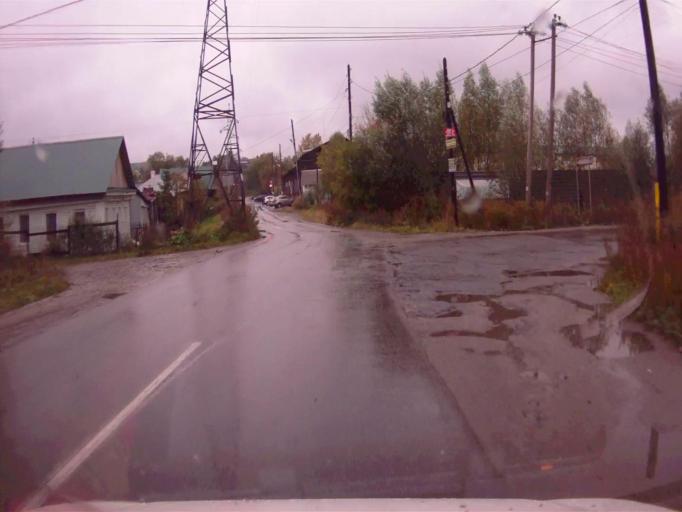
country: RU
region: Chelyabinsk
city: Kyshtym
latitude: 55.7155
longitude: 60.5436
